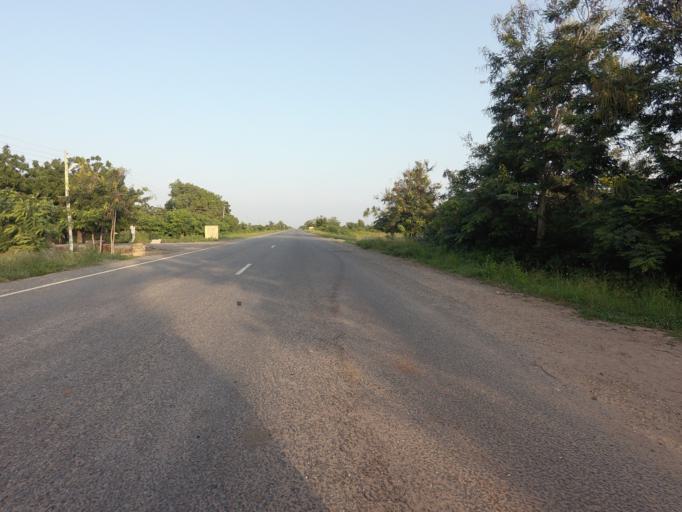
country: GH
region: Volta
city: Anloga
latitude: 5.8917
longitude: 0.7184
